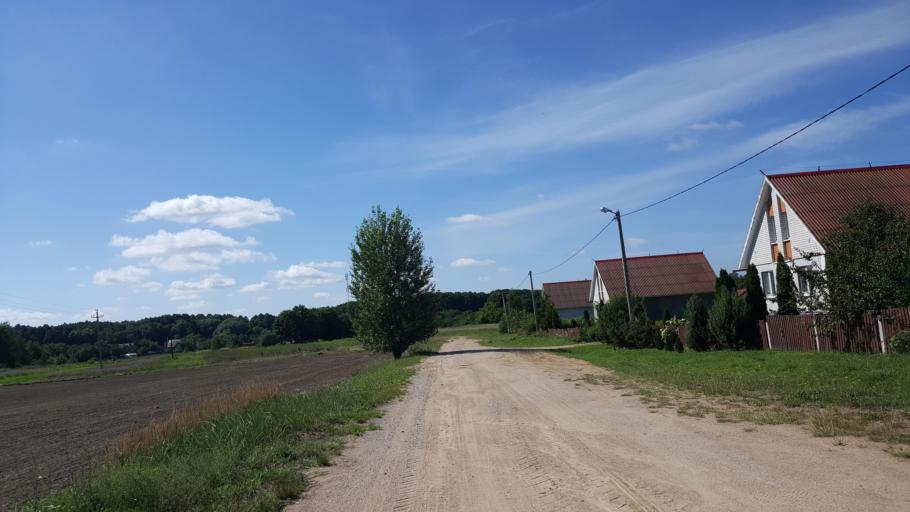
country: BY
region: Brest
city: Charnawchytsy
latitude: 52.2773
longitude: 23.7735
